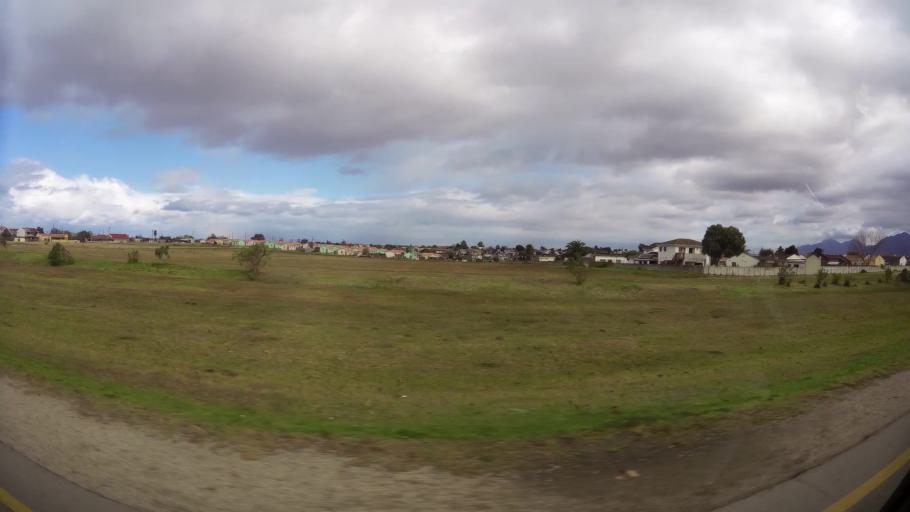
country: ZA
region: Western Cape
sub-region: Eden District Municipality
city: George
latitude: -33.9732
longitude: 22.4912
